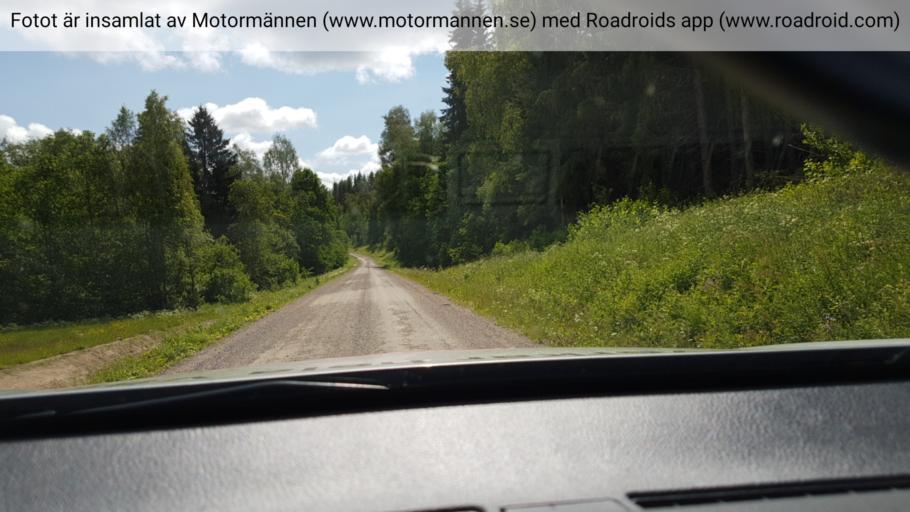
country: SE
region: Vaermland
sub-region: Hagfors Kommun
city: Ekshaerad
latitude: 60.3671
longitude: 13.2955
